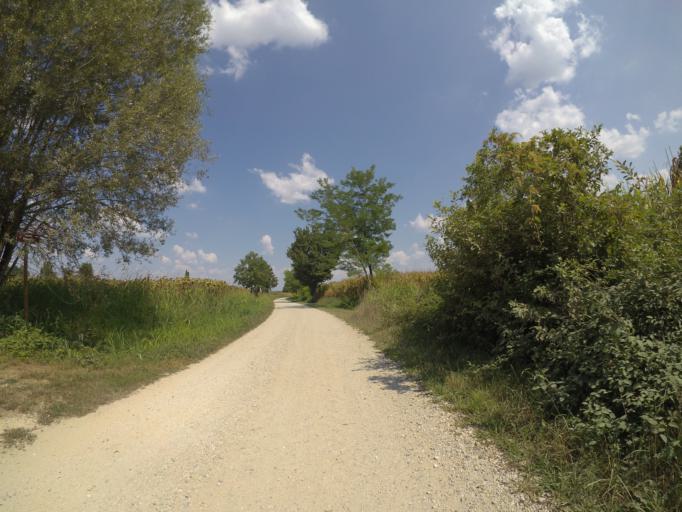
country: IT
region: Friuli Venezia Giulia
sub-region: Provincia di Udine
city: Bertiolo
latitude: 45.9292
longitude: 13.0800
